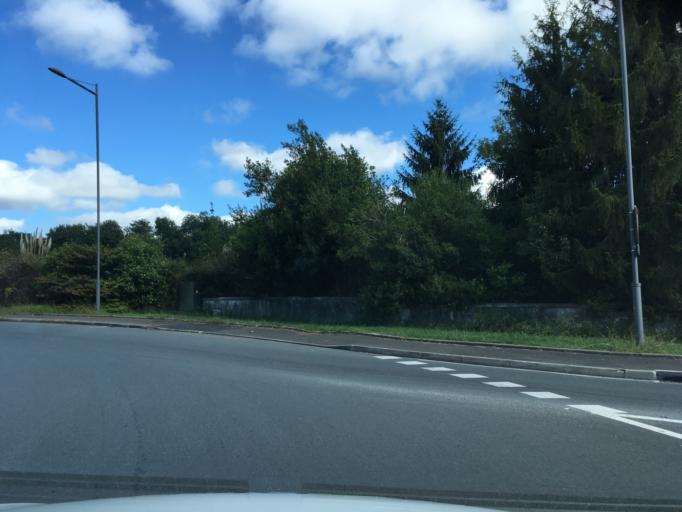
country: FR
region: Aquitaine
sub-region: Departement des Pyrenees-Atlantiques
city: Boucau
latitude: 43.5025
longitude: -1.4559
